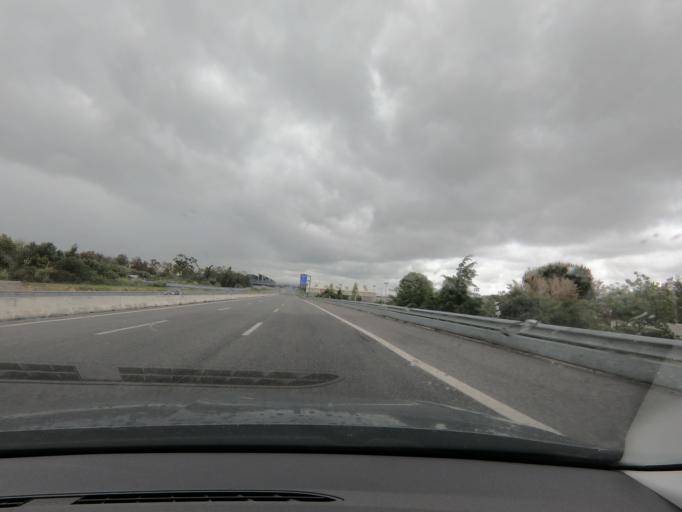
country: PT
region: Lisbon
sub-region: Sintra
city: Sintra
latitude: 38.7626
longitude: -9.3763
